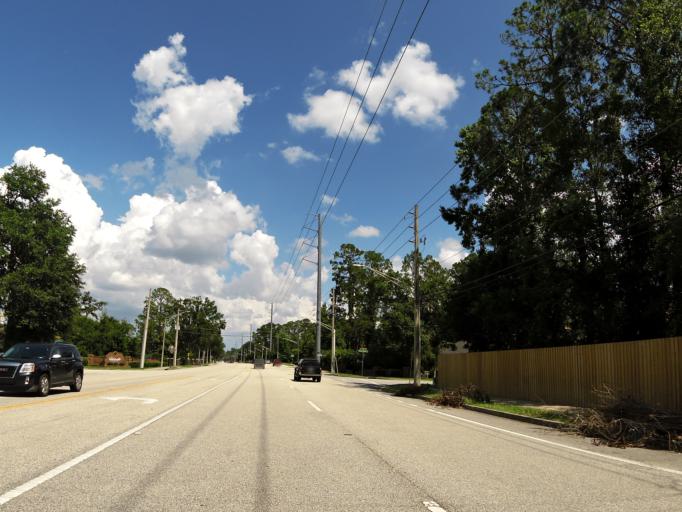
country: US
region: Florida
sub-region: Saint Johns County
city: Fruit Cove
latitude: 30.1568
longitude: -81.5941
